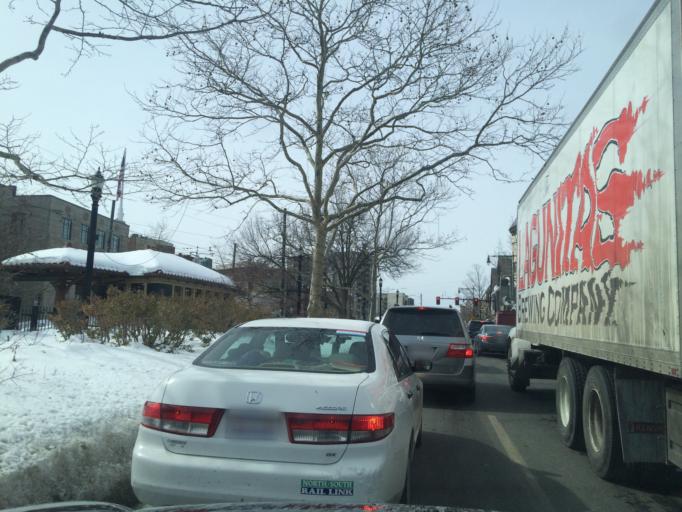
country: US
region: Massachusetts
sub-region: Norfolk County
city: Brookline
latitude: 42.3425
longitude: -71.1204
